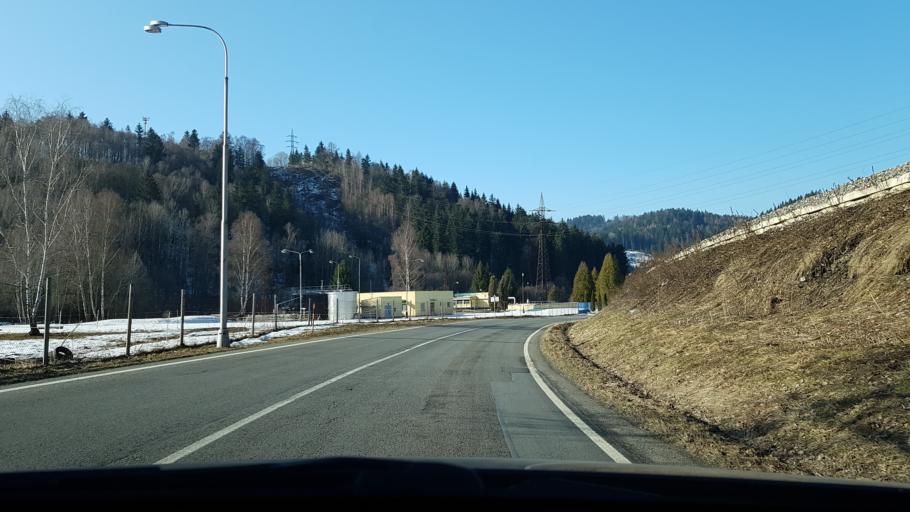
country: CZ
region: Olomoucky
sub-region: Okres Sumperk
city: Hanusovice
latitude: 50.0960
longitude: 16.9875
